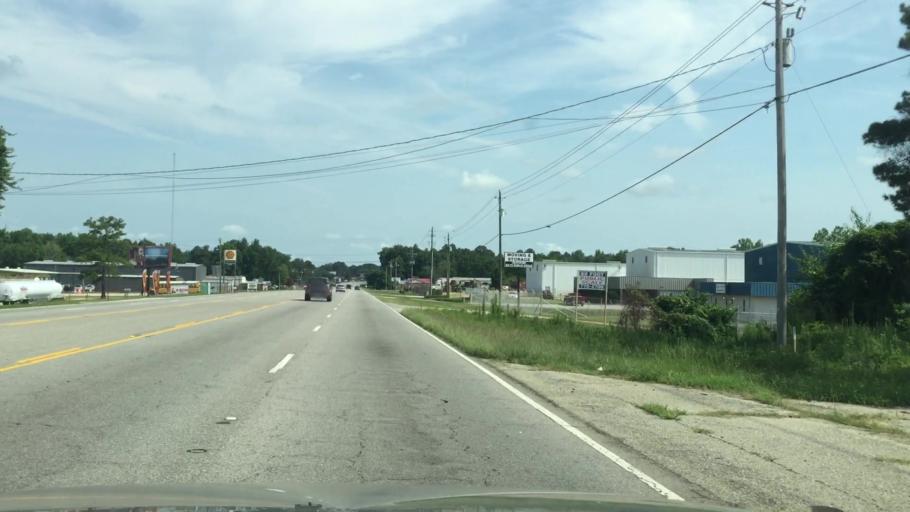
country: US
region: South Carolina
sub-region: Sumter County
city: South Sumter
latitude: 33.8931
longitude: -80.3518
